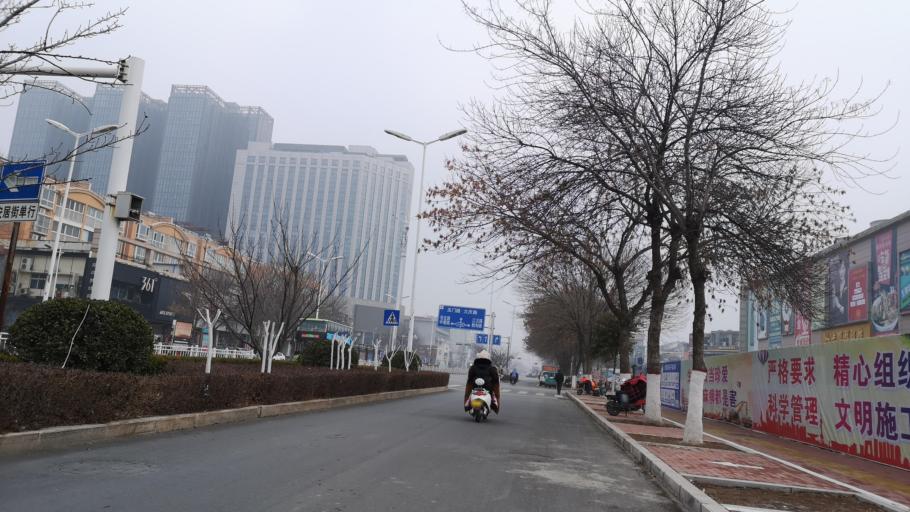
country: CN
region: Henan Sheng
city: Zhongyuanlu
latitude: 35.7708
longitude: 115.0564
